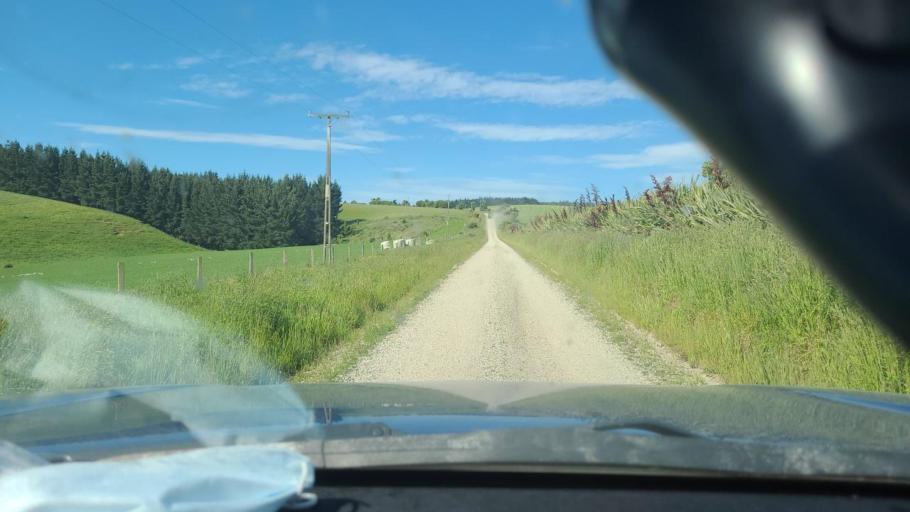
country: NZ
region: Southland
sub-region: Gore District
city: Gore
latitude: -46.5042
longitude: 168.8199
